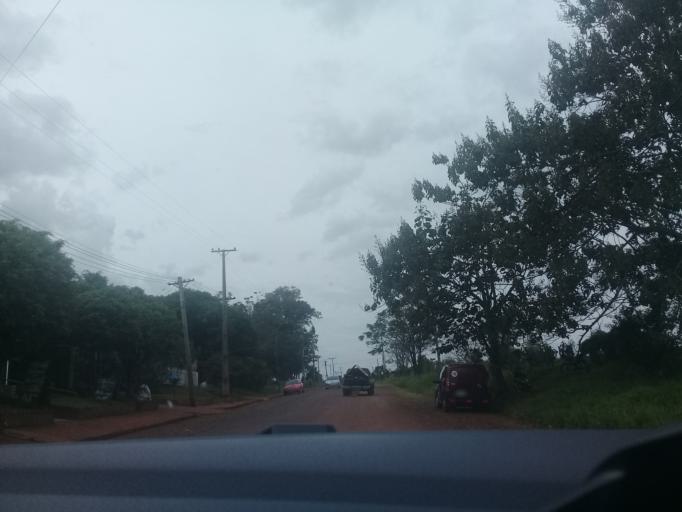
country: AR
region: Misiones
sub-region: Departamento de Obera
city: Obera
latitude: -27.4836
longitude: -55.1514
